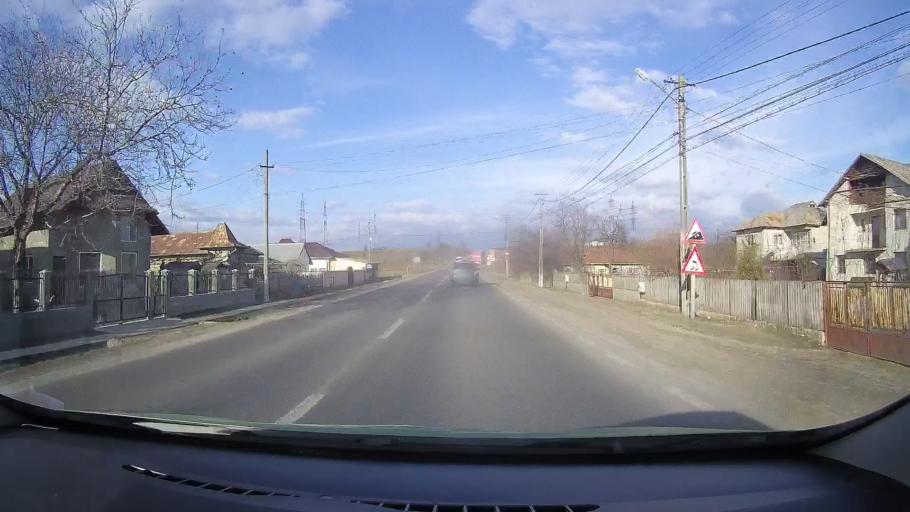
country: RO
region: Dambovita
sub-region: Comuna Ulmi
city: Viisoara
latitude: 44.8817
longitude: 25.4282
